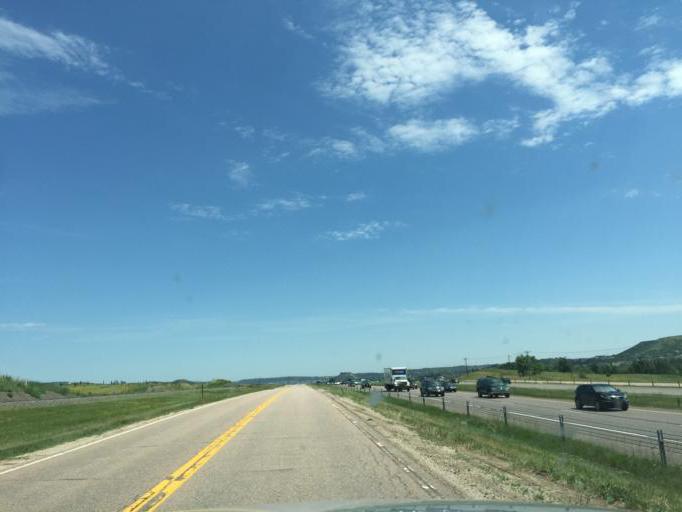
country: US
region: Colorado
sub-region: Douglas County
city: Castle Rock
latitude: 39.3230
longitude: -104.8821
